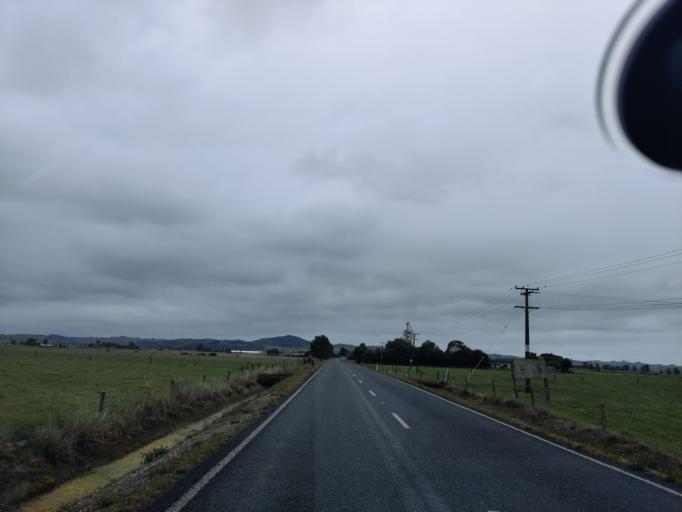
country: NZ
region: Northland
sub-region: Kaipara District
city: Dargaville
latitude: -36.1221
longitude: 174.0536
